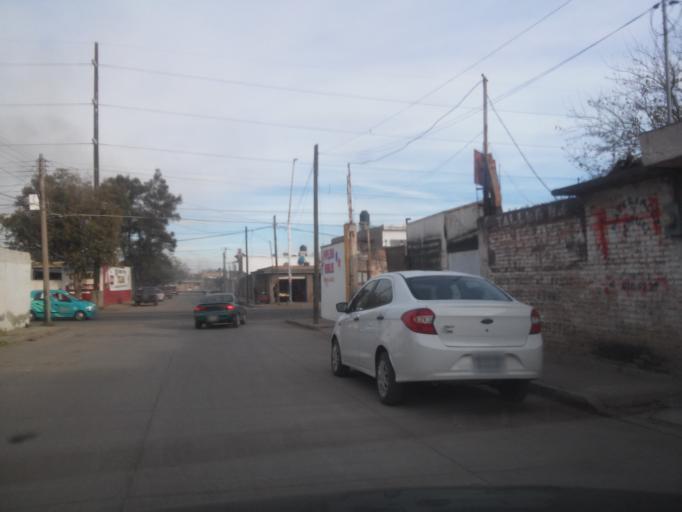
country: MX
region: Durango
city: Victoria de Durango
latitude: 24.0184
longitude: -104.6331
